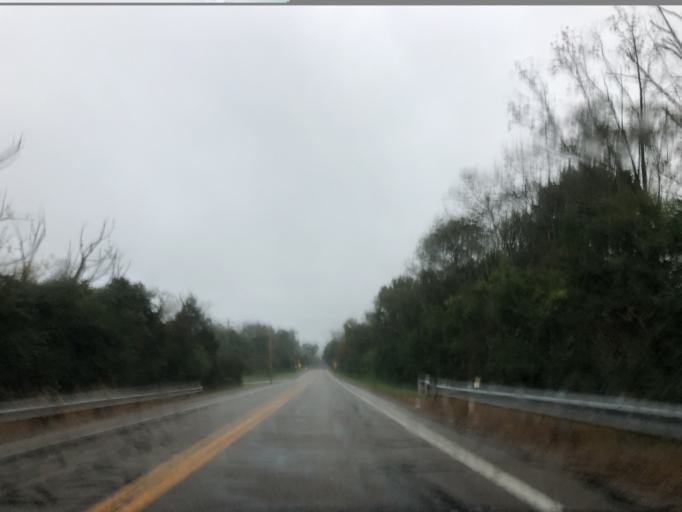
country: US
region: Ohio
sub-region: Hamilton County
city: The Village of Indian Hill
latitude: 39.2487
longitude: -84.3047
